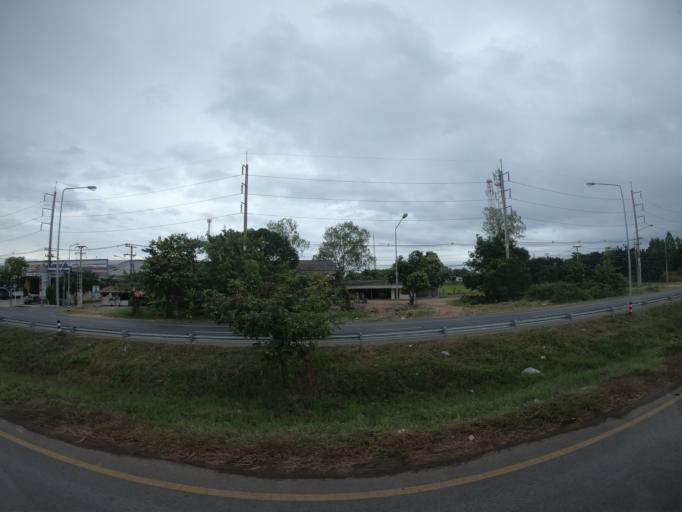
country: TH
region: Roi Et
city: Roi Et
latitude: 16.0482
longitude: 103.6216
